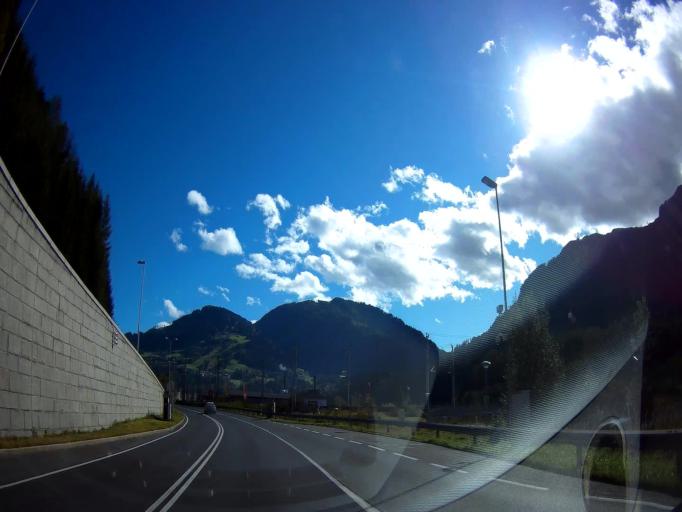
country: AT
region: Salzburg
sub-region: Politischer Bezirk Sankt Johann im Pongau
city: Schwarzach im Pongau
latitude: 47.3219
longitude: 13.1561
